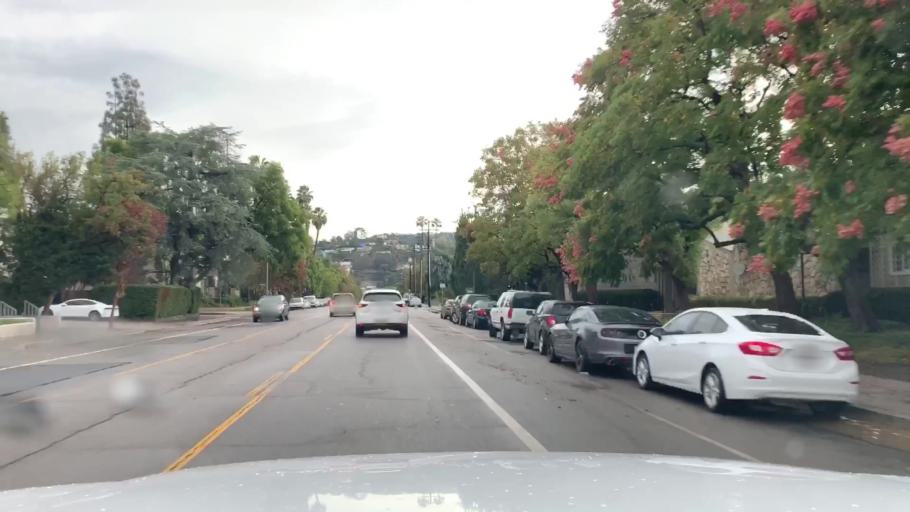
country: US
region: California
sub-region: Los Angeles County
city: North Hollywood
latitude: 34.1492
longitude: -118.3877
